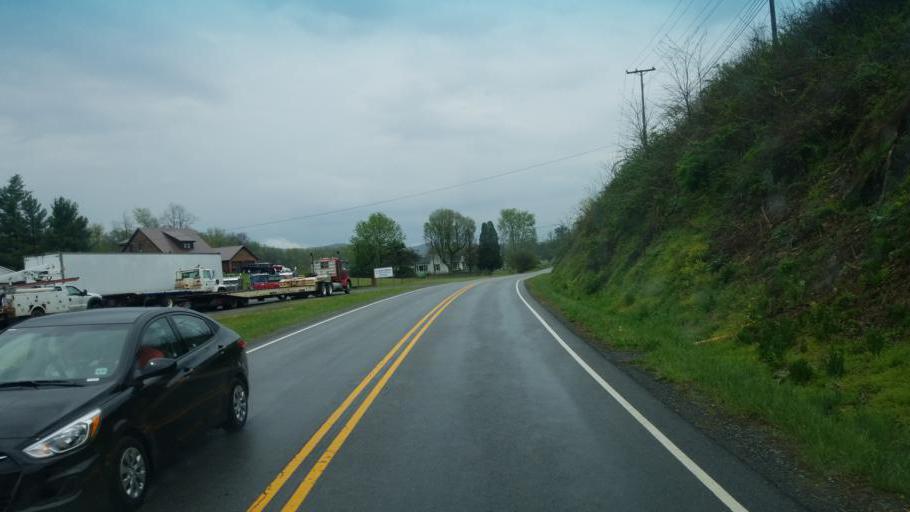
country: US
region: Virginia
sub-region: Smyth County
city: Atkins
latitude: 36.8828
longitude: -81.3791
